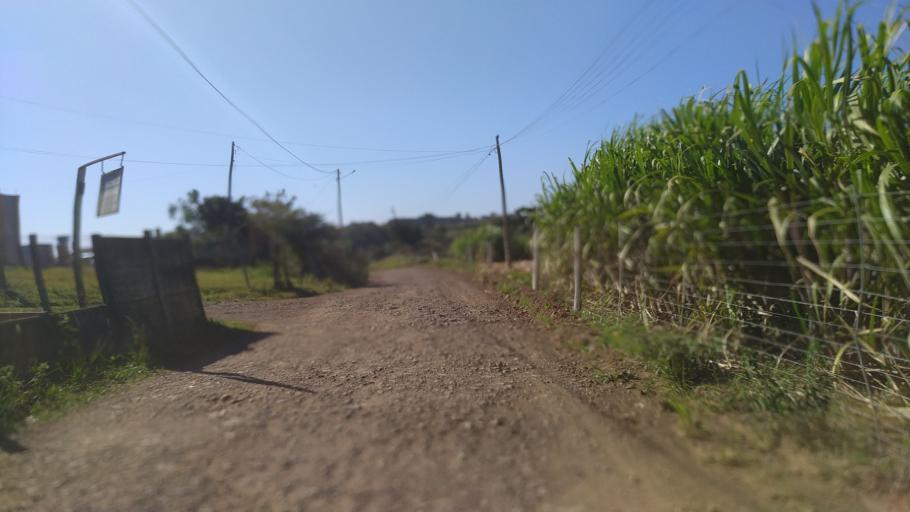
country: BR
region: Santa Catarina
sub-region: Chapeco
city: Chapeco
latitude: -27.1499
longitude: -52.5964
